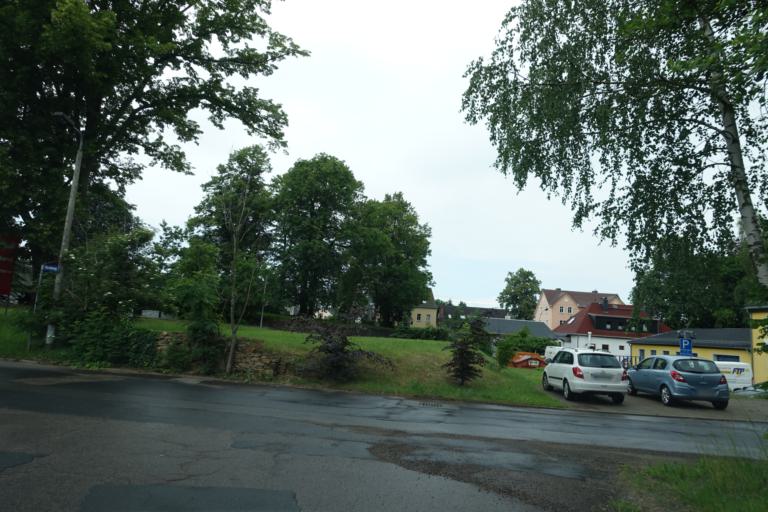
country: DE
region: Saxony
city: Brand-Erbisdorf
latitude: 50.8600
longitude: 13.3206
